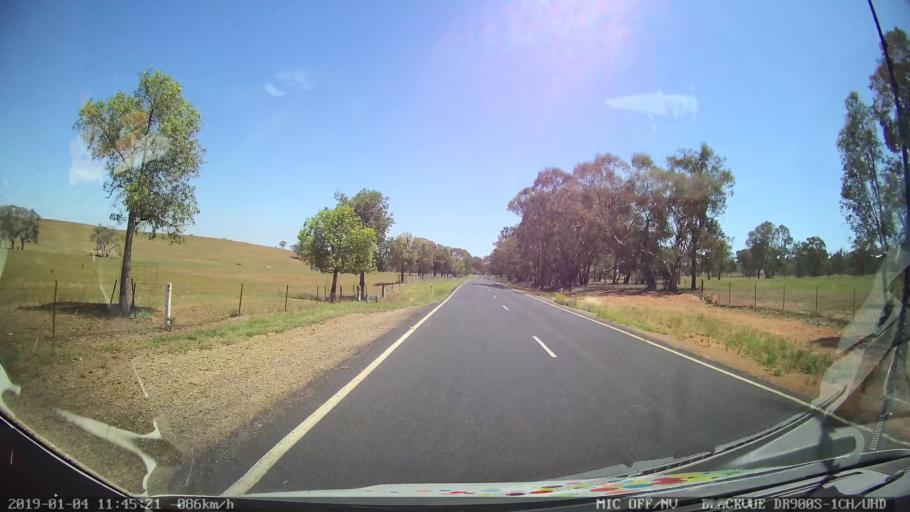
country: AU
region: New South Wales
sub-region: Cabonne
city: Molong
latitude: -32.9549
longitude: 148.7638
